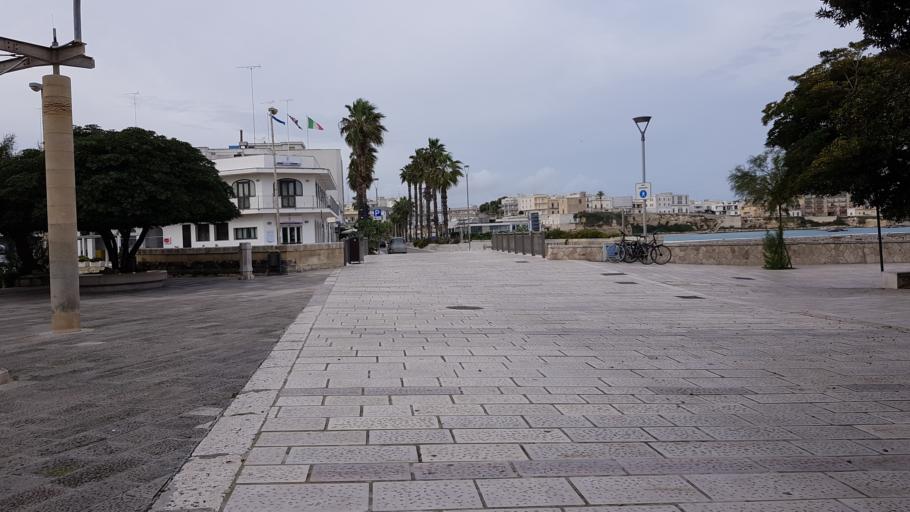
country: IT
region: Apulia
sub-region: Provincia di Lecce
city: Otranto
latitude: 40.1462
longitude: 18.4889
